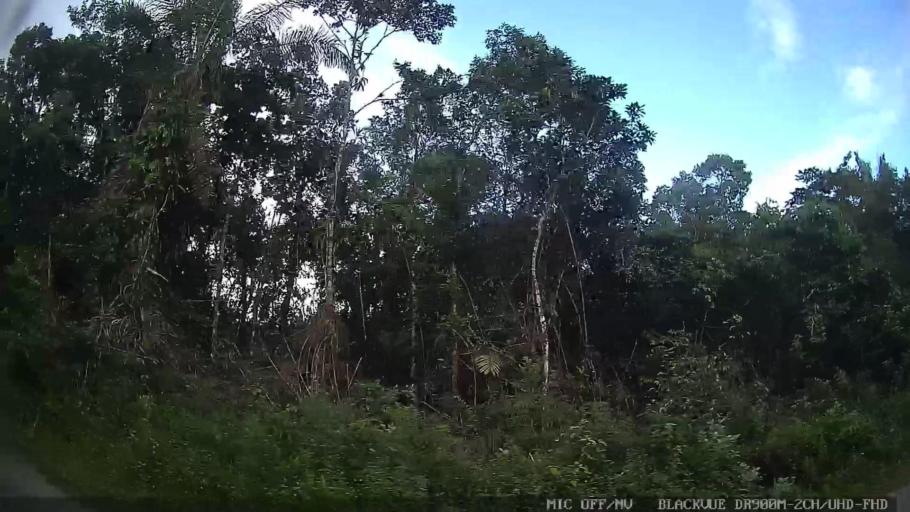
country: BR
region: Sao Paulo
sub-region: Peruibe
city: Peruibe
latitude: -24.1920
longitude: -46.9408
